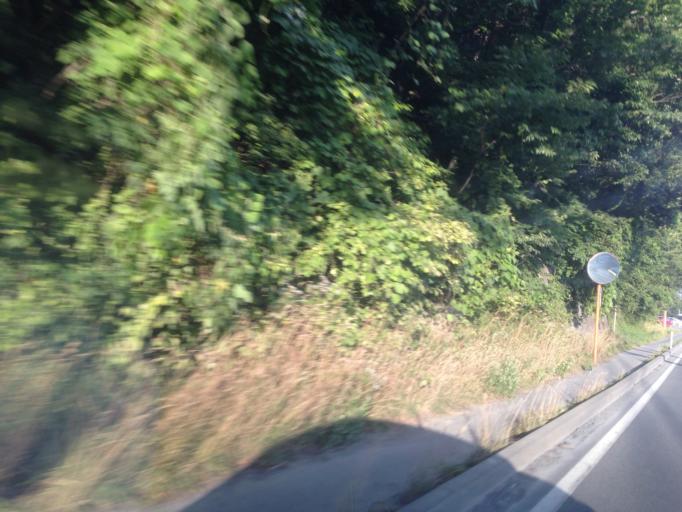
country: JP
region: Iwate
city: Otsuchi
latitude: 39.3719
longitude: 141.8926
